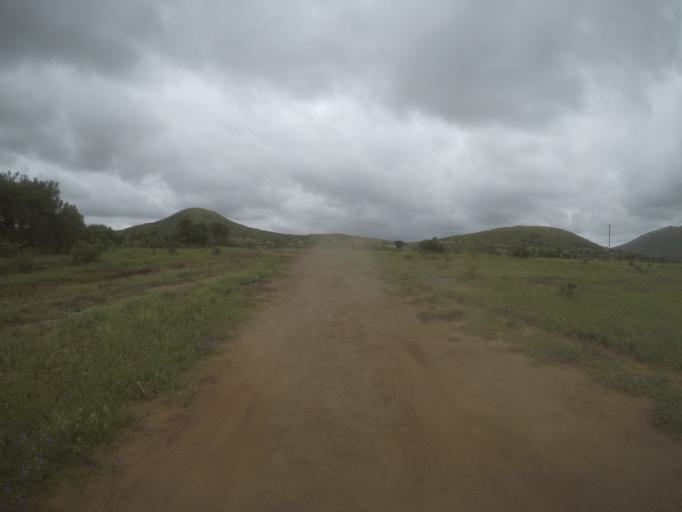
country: ZA
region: KwaZulu-Natal
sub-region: uThungulu District Municipality
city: Empangeni
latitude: -28.6059
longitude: 31.8653
